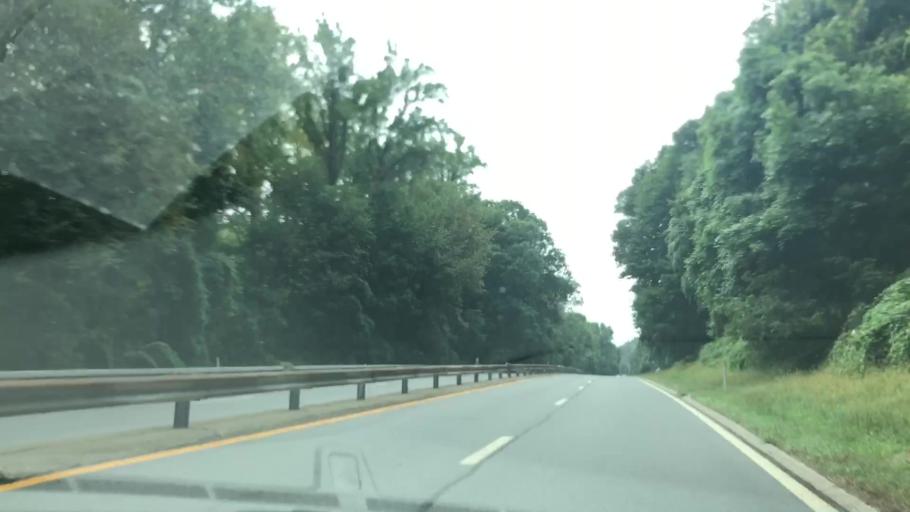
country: US
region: New York
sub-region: Westchester County
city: Hastings-on-Hudson
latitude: 40.9942
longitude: -73.8617
